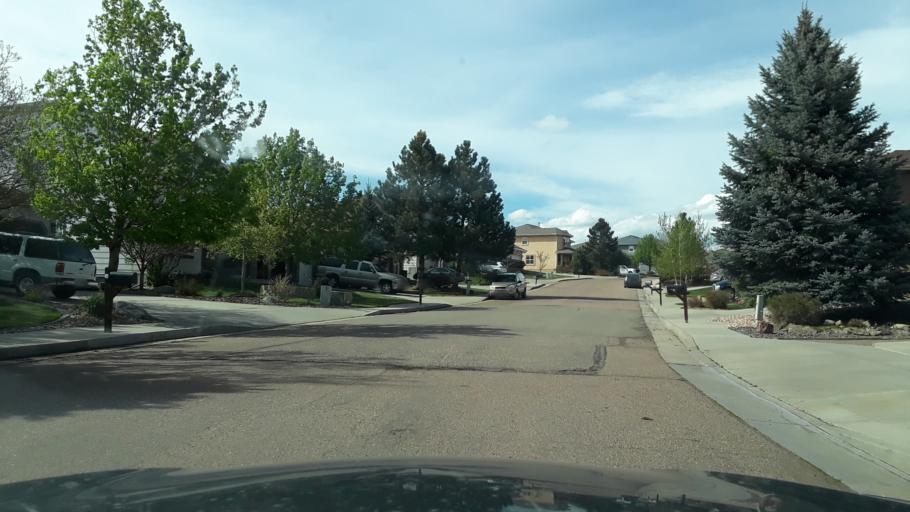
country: US
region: Colorado
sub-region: El Paso County
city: Gleneagle
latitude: 39.0081
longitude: -104.7985
